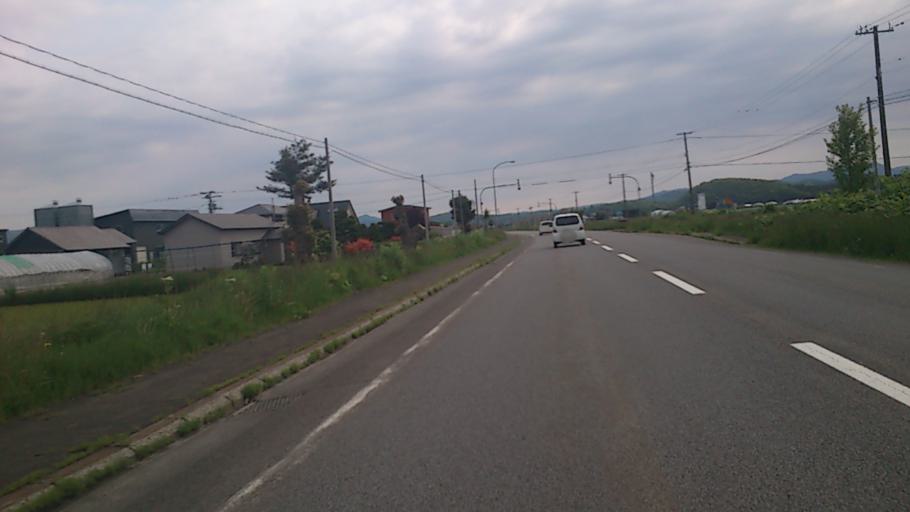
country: JP
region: Hokkaido
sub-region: Asahikawa-shi
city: Asahikawa
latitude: 43.8582
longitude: 142.5094
